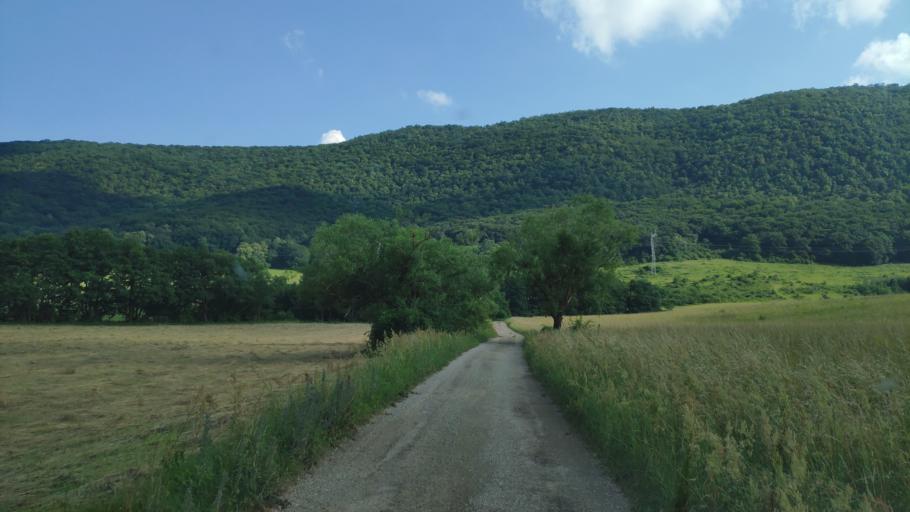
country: HU
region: Borsod-Abauj-Zemplen
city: Szendro
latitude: 48.5878
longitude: 20.7302
